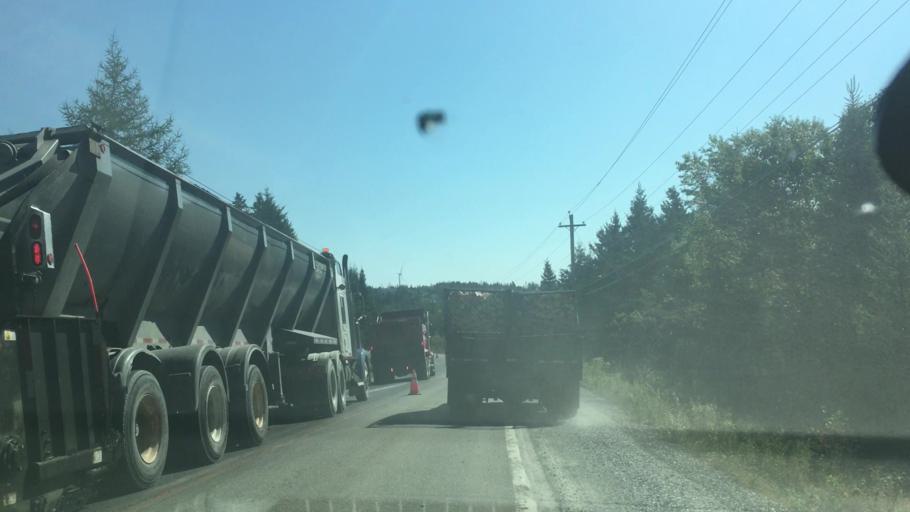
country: CA
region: Nova Scotia
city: New Glasgow
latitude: 44.9077
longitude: -62.4975
